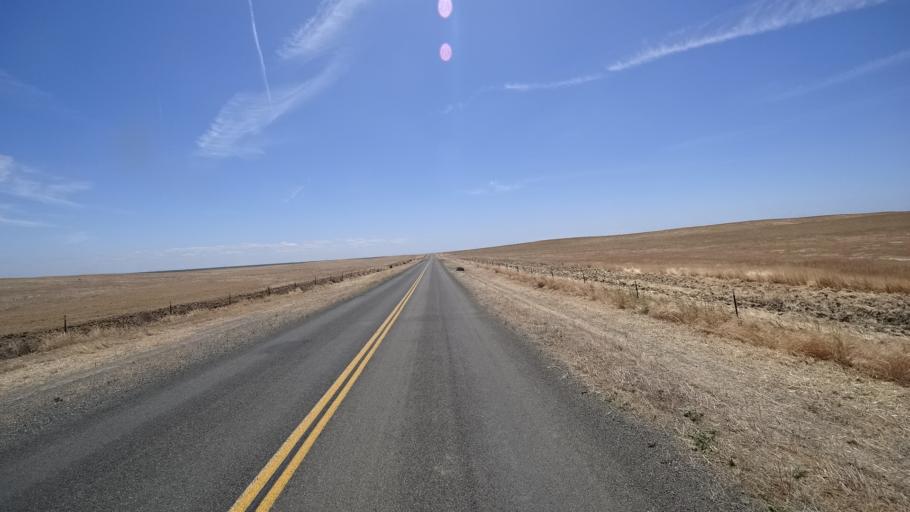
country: US
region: California
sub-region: Kings County
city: Kettleman City
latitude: 35.8173
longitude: -119.9043
